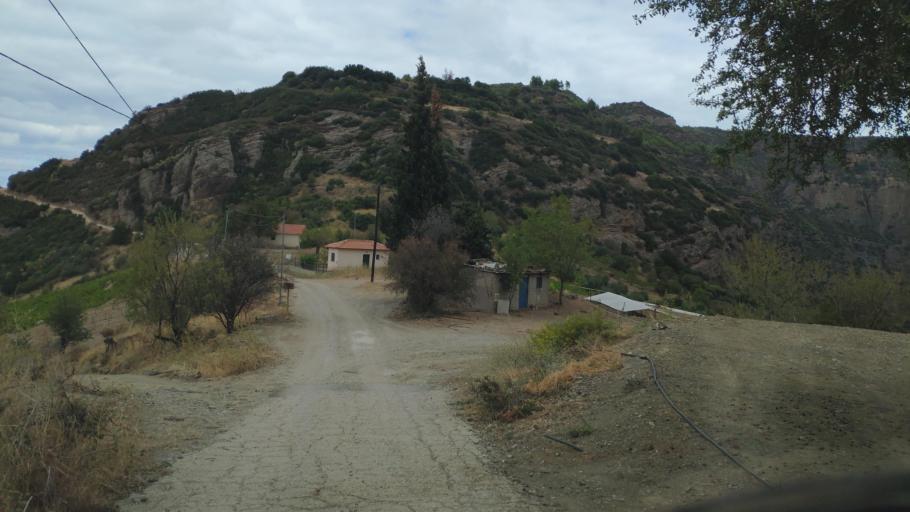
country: GR
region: West Greece
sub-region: Nomos Achaias
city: Temeni
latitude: 38.1572
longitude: 22.1418
